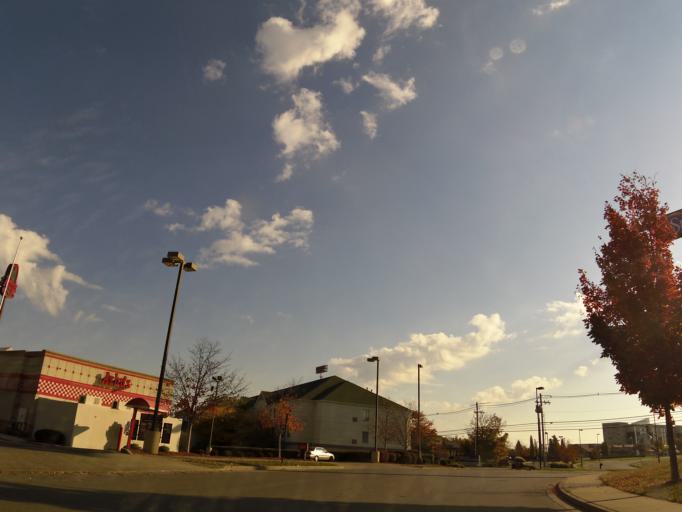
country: US
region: Kentucky
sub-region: Fayette County
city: Lexington-Fayette
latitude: 38.0196
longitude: -84.4146
